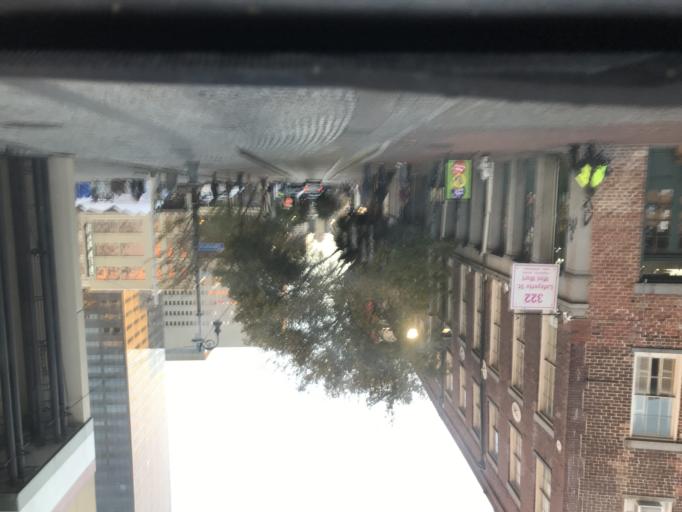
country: US
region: Louisiana
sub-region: Orleans Parish
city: New Orleans
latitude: 29.9474
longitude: -90.0665
